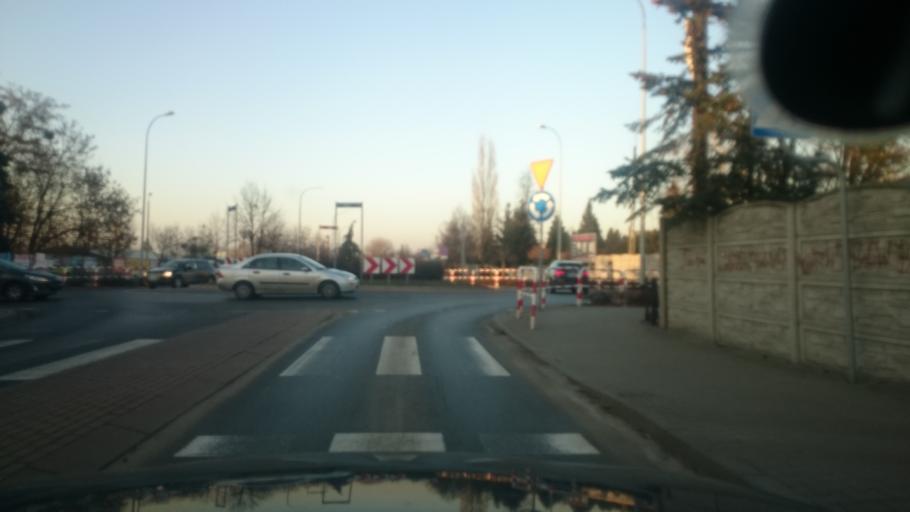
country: PL
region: Greater Poland Voivodeship
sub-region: Powiat ostrowski
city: Ostrow Wielkopolski
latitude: 51.6494
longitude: 17.8376
